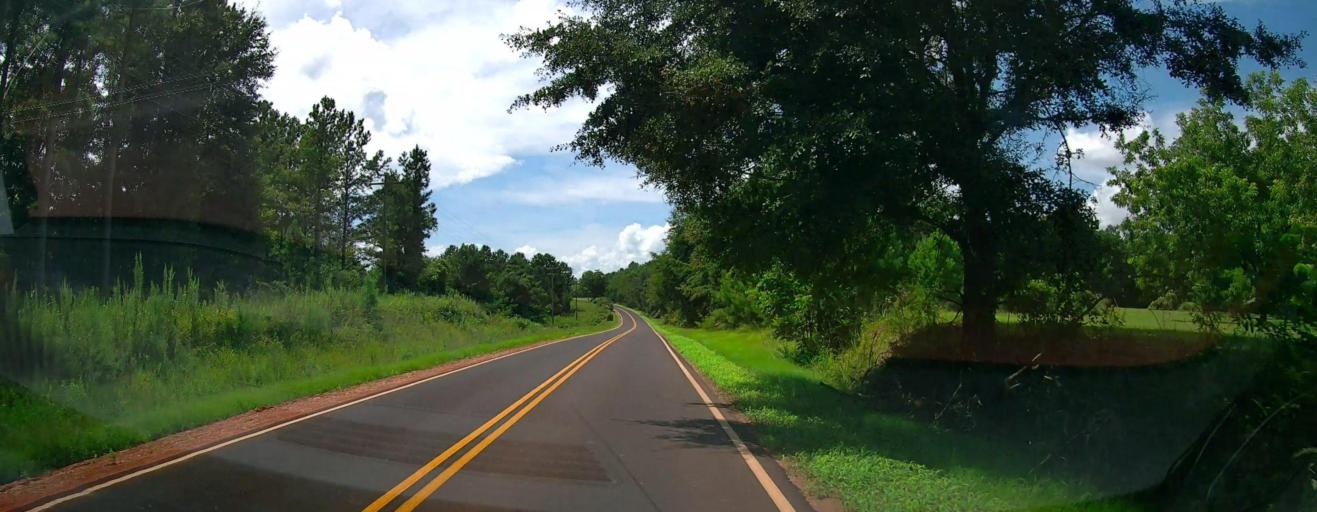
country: US
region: Georgia
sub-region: Macon County
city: Marshallville
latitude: 32.4588
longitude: -83.9146
